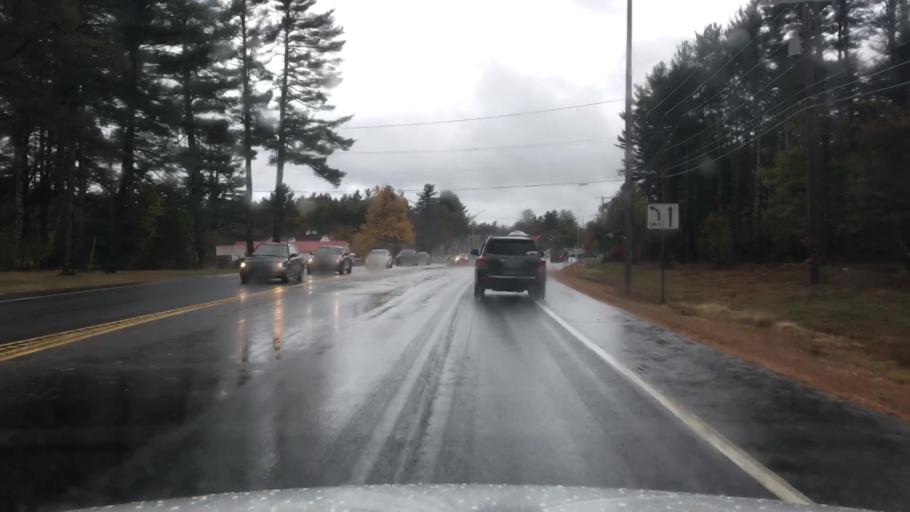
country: US
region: New Hampshire
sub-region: Strafford County
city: Barrington
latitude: 43.2149
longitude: -70.9948
